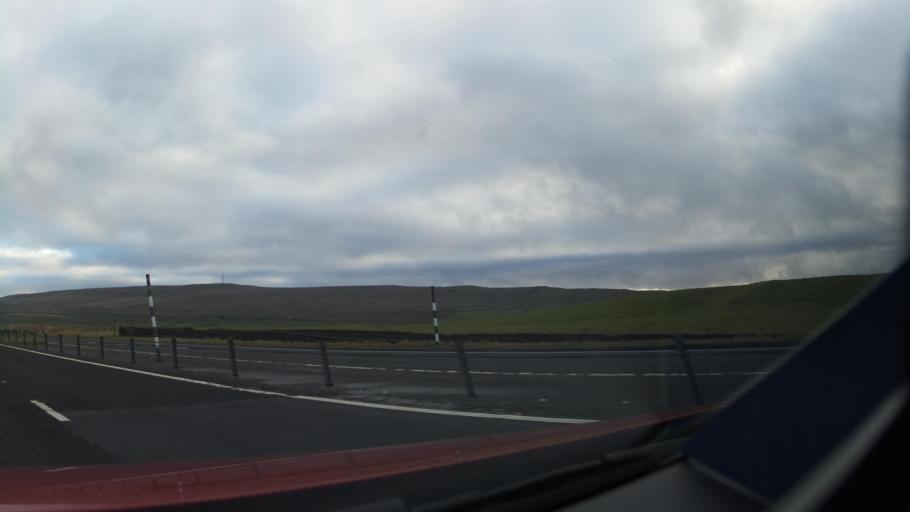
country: GB
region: England
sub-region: Cumbria
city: Kirkby Stephen
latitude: 54.5211
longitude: -2.2207
